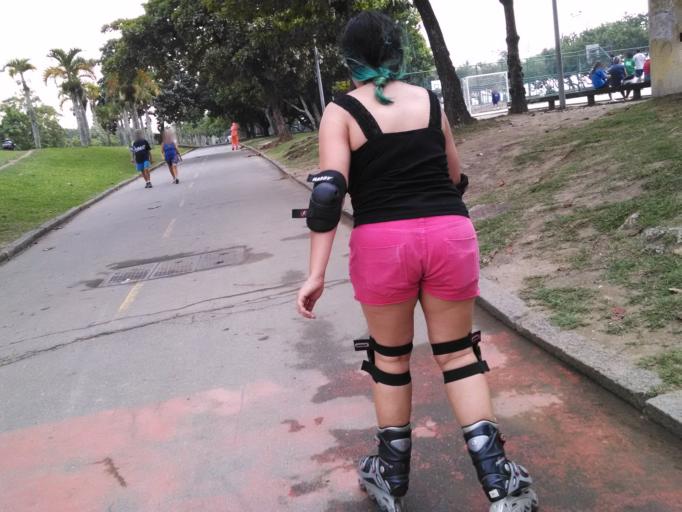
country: BR
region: Rio de Janeiro
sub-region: Rio De Janeiro
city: Rio de Janeiro
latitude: -22.9300
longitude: -43.1725
